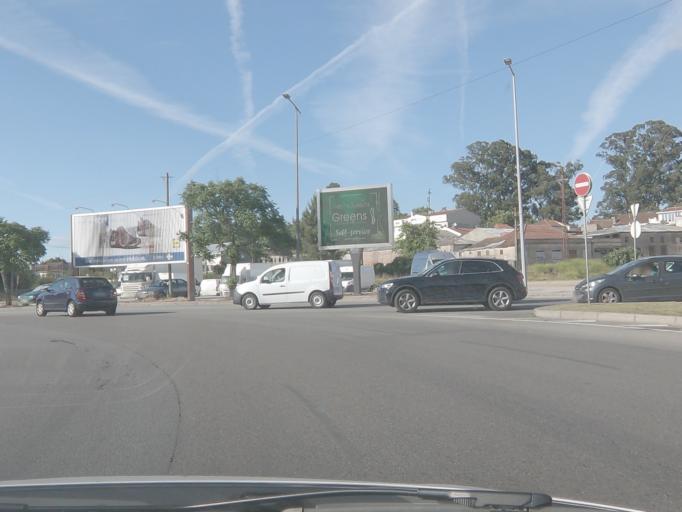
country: PT
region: Viseu
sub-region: Viseu
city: Viseu
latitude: 40.6645
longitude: -7.9162
